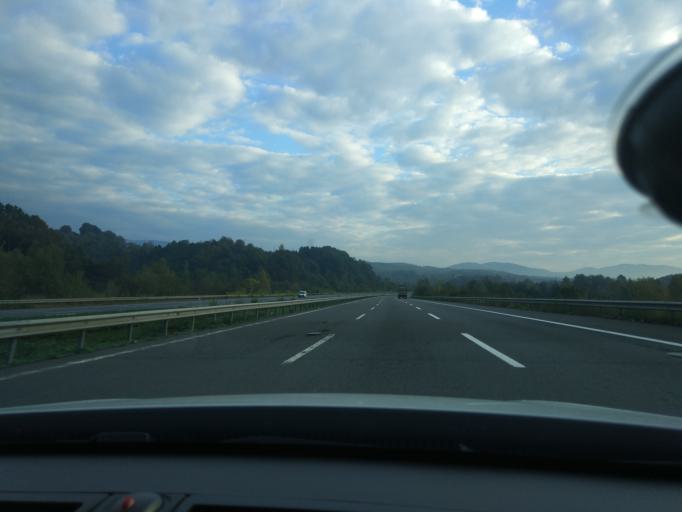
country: TR
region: Sakarya
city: Hendek
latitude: 40.7733
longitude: 30.7838
